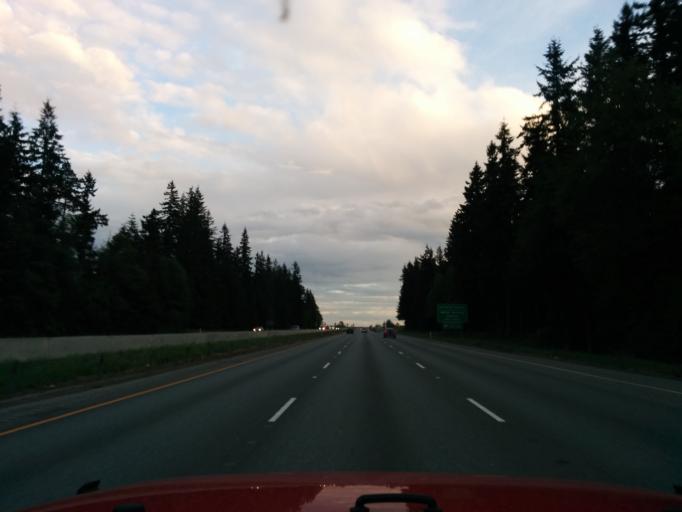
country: US
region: Washington
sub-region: Snohomish County
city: Smokey Point
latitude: 48.1631
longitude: -122.1909
